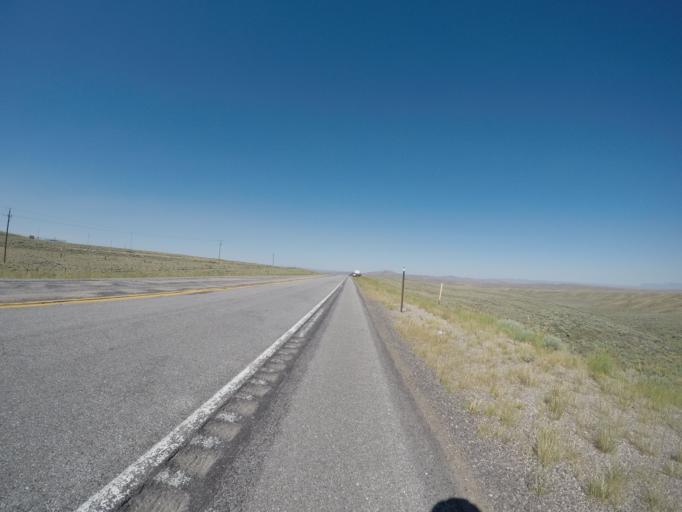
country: US
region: Wyoming
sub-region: Carbon County
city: Saratoga
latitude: 41.7946
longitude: -106.7376
